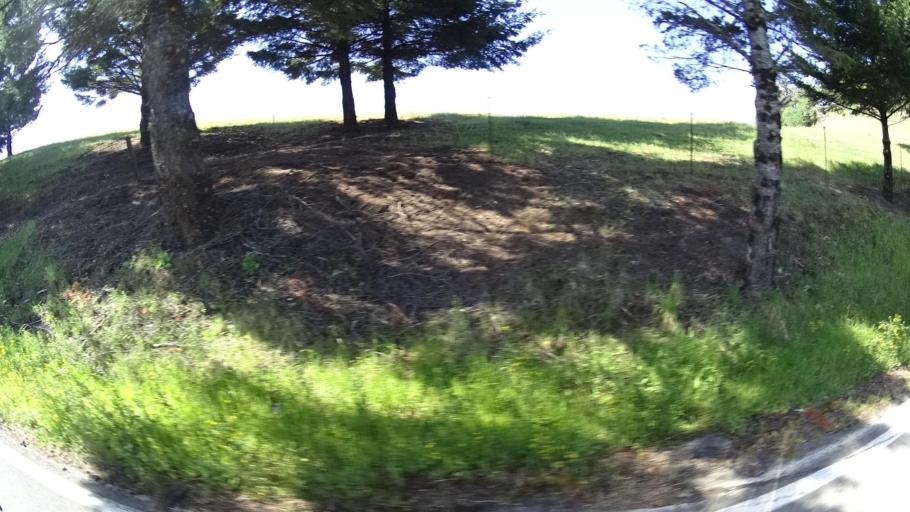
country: US
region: California
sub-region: Humboldt County
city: Redway
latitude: 40.1083
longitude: -123.7506
